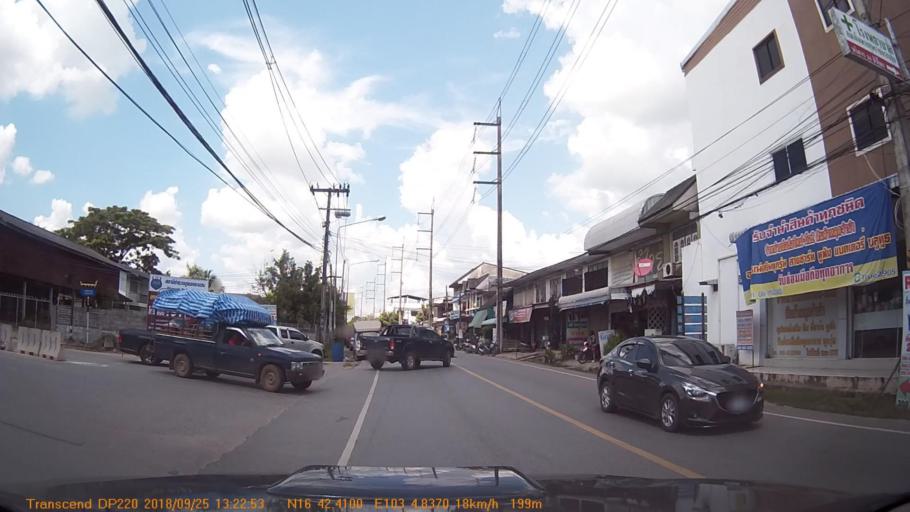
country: TH
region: Khon Kaen
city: Kranuan
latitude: 16.7069
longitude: 103.0807
